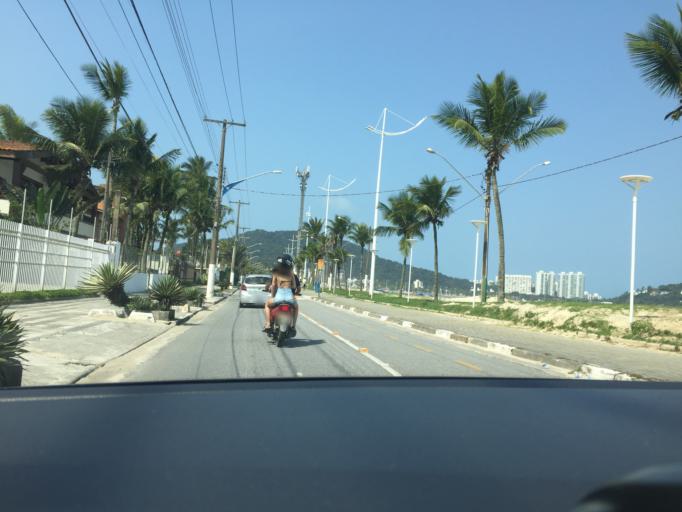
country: BR
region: Sao Paulo
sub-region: Guaruja
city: Guaruja
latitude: -23.9848
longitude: -46.2166
